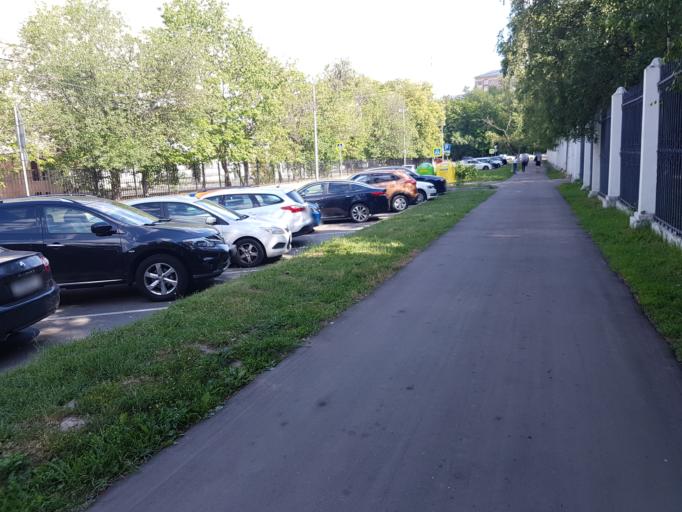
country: RU
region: Moskovskaya
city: Koptevo
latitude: 55.8207
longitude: 37.5038
